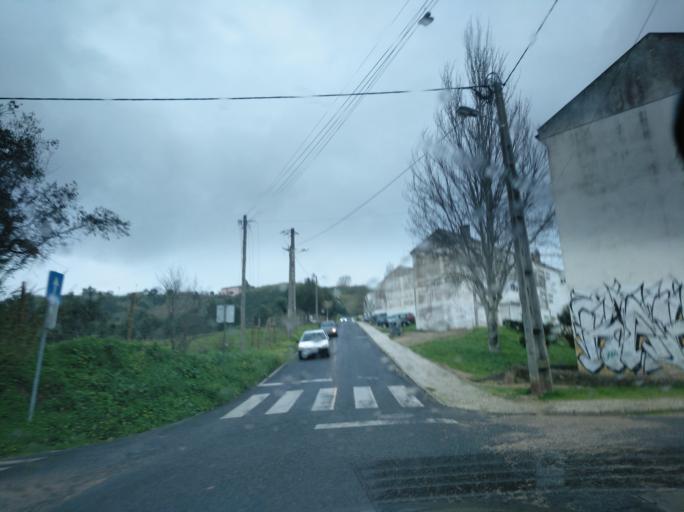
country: PT
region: Lisbon
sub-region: Odivelas
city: Pontinha
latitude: 38.7740
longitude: -9.1962
